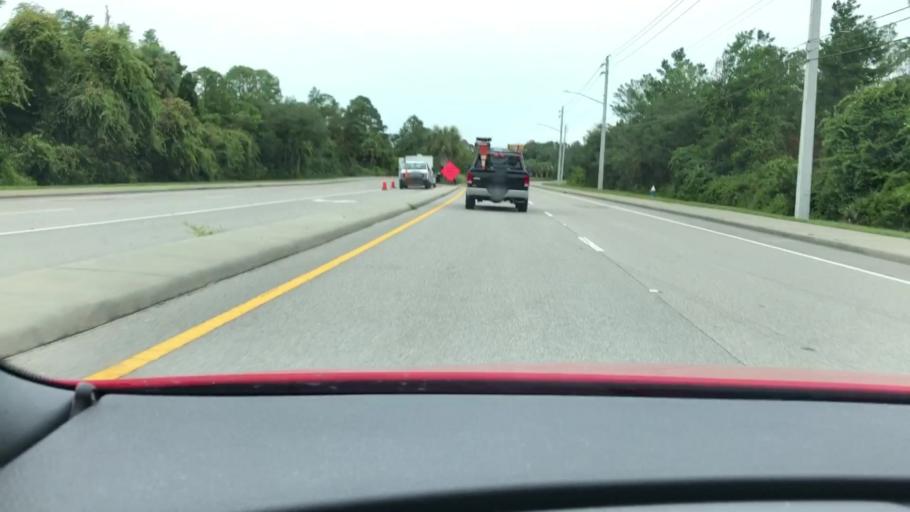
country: US
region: Florida
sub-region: Flagler County
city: Flagler Beach
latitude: 29.4889
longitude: -81.1867
